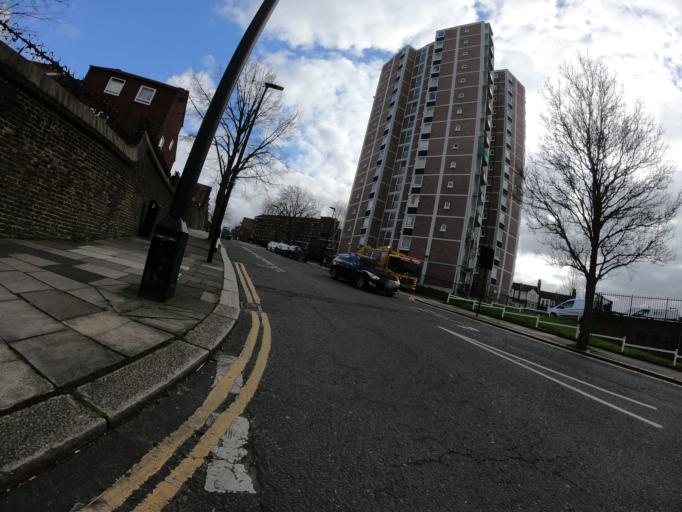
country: GB
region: England
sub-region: Greater London
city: Woolwich
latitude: 51.4899
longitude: 0.0532
